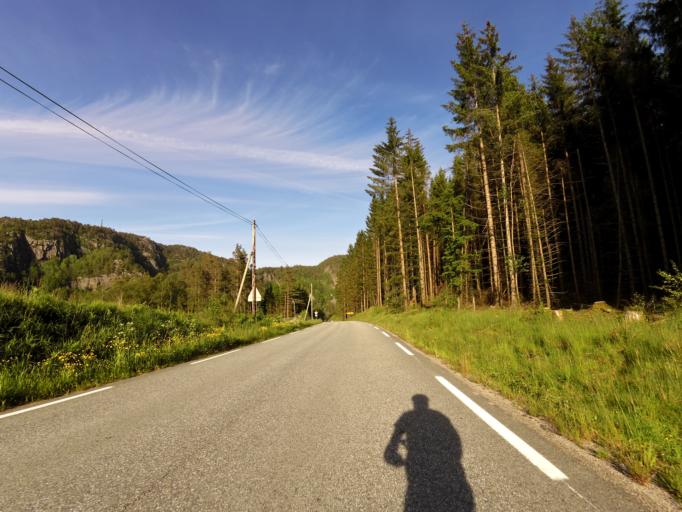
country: NO
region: Vest-Agder
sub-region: Flekkefjord
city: Flekkefjord
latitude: 58.2861
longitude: 6.6067
